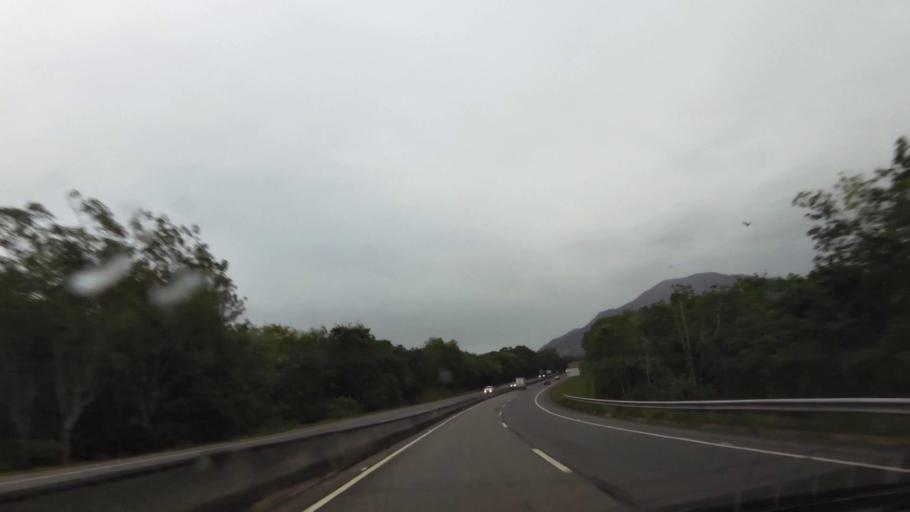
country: BR
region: Espirito Santo
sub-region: Guarapari
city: Guarapari
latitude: -20.6308
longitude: -40.5102
